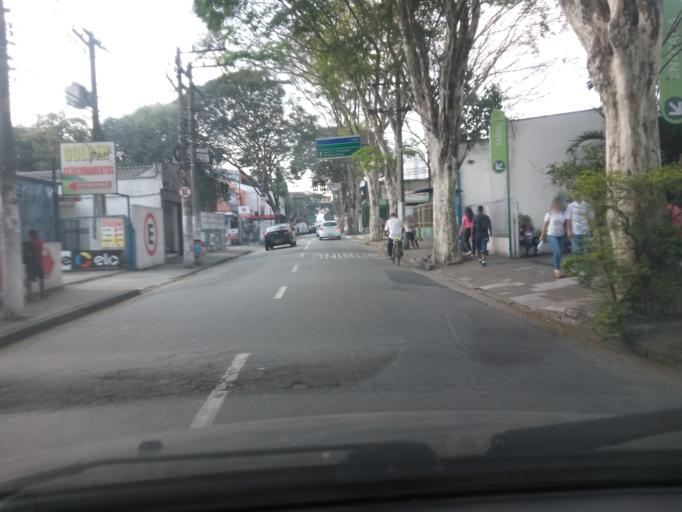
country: BR
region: Sao Paulo
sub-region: Sao Bernardo Do Campo
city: Sao Bernardo do Campo
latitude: -23.7051
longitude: -46.5507
